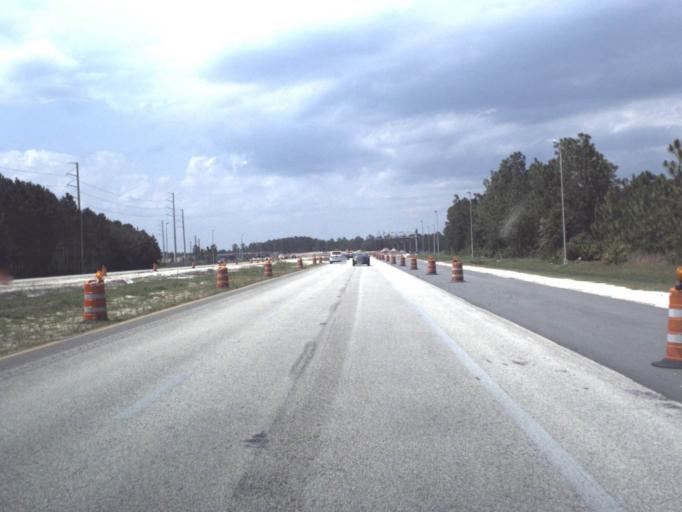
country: US
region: Florida
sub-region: Clay County
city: Bellair-Meadowbrook Terrace
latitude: 30.2365
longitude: -81.8437
